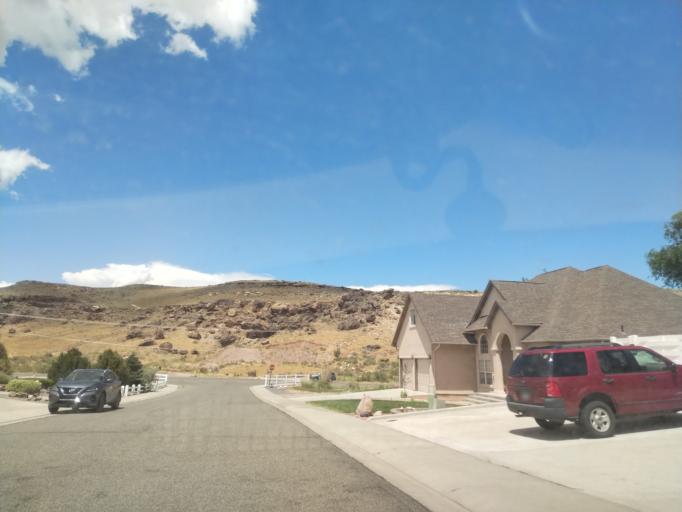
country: US
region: Colorado
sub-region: Mesa County
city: Redlands
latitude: 39.0718
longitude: -108.6462
